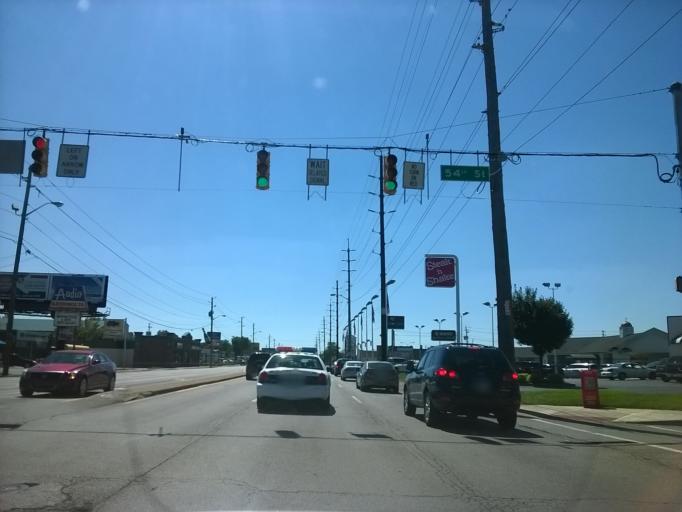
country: US
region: Indiana
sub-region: Marion County
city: Broad Ripple
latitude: 39.8514
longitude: -86.1223
